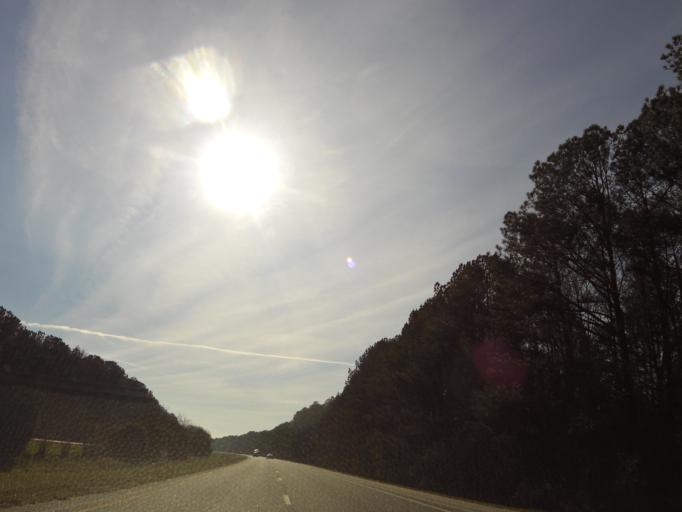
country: US
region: Georgia
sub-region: Harris County
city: Pine Mountain
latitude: 32.8505
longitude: -84.9885
